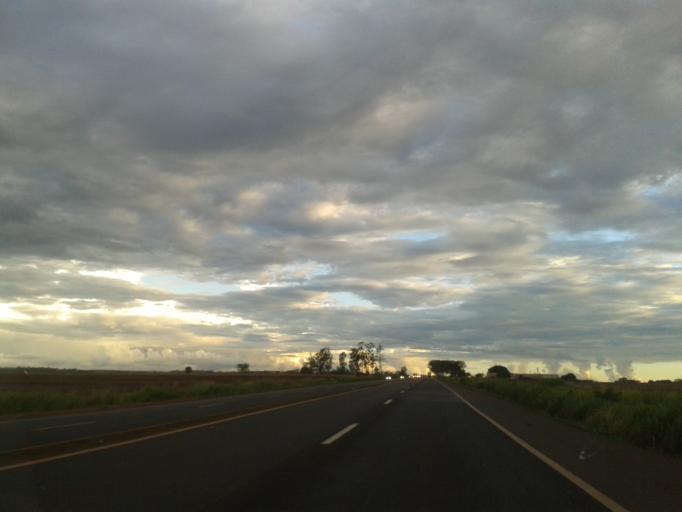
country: BR
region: Minas Gerais
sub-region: Centralina
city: Centralina
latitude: -18.5614
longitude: -49.1939
